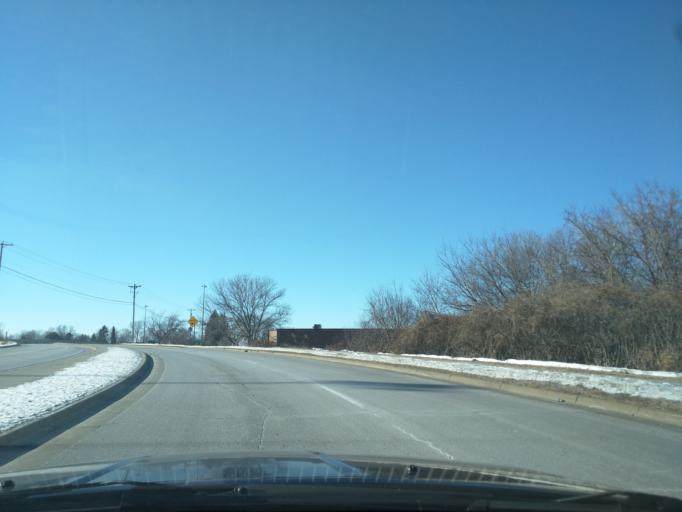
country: US
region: Minnesota
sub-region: Hennepin County
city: Edina
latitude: 44.8610
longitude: -93.3831
